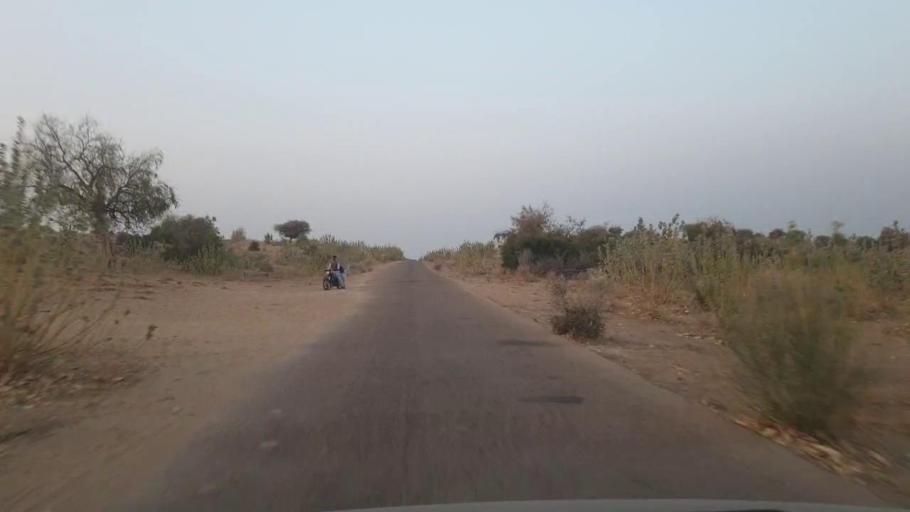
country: PK
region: Sindh
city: Umarkot
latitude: 25.3304
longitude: 70.0577
